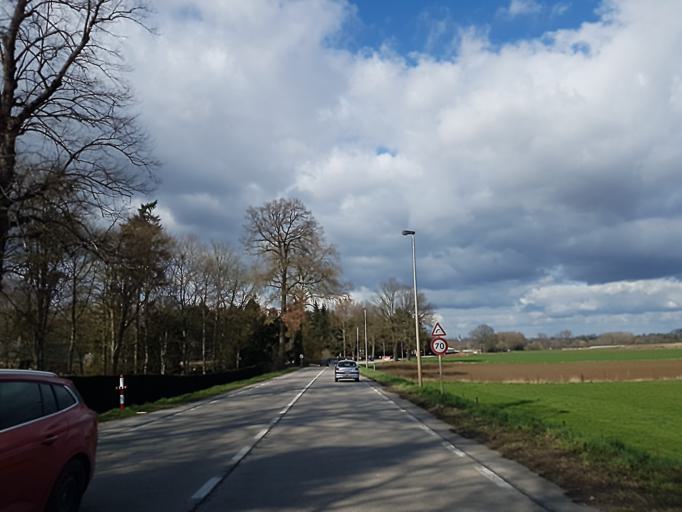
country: BE
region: Wallonia
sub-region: Province du Brabant Wallon
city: Jodoigne
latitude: 50.7034
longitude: 4.8505
